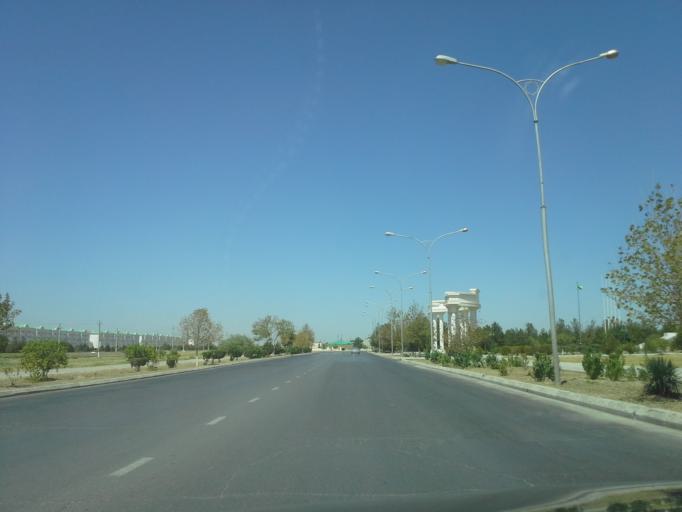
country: TM
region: Ahal
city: Ashgabat
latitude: 37.9903
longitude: 58.3236
